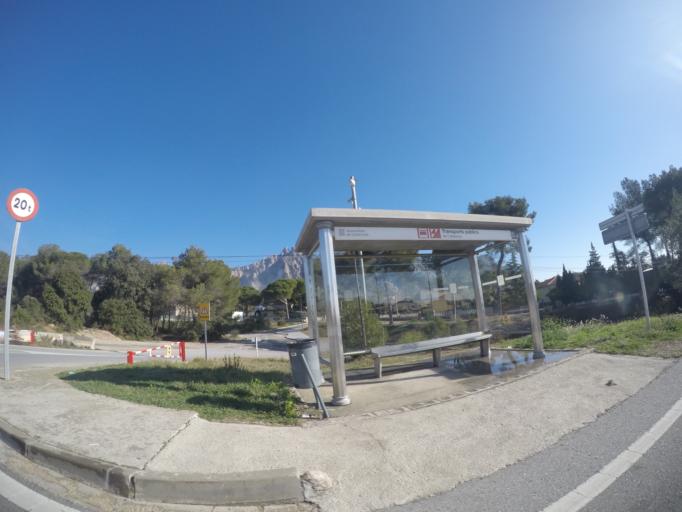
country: ES
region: Catalonia
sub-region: Provincia de Barcelona
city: Collbato
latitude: 41.5675
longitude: 1.8080
